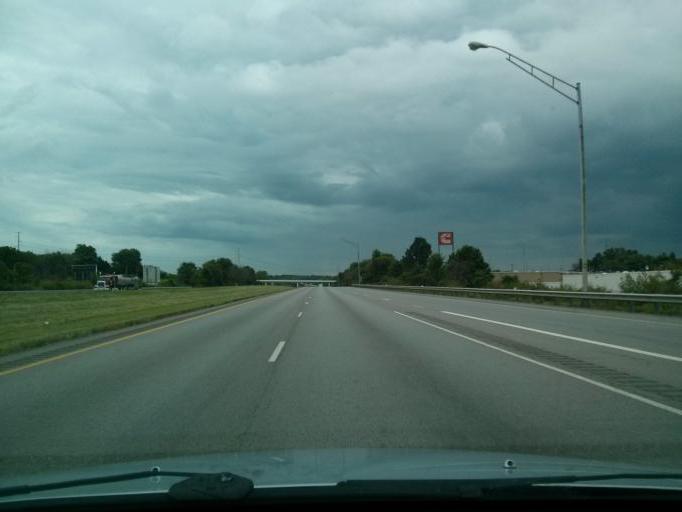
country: US
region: Ohio
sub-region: Trumbull County
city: Hubbard
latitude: 41.1764
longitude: -80.5615
